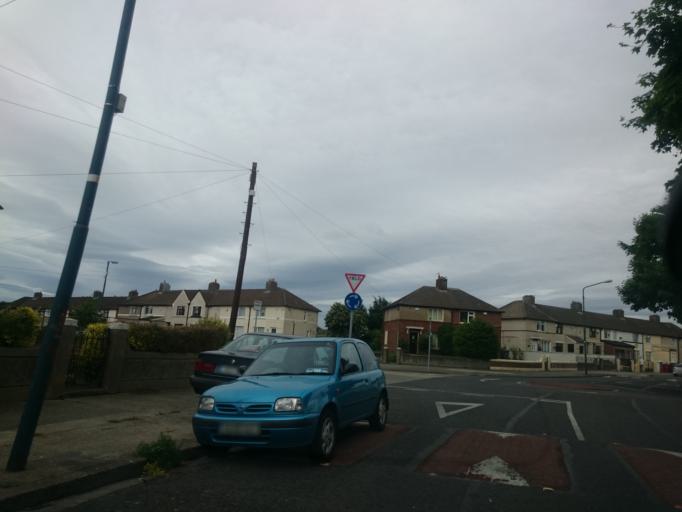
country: IE
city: Greenhills
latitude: 53.3233
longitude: -6.2988
